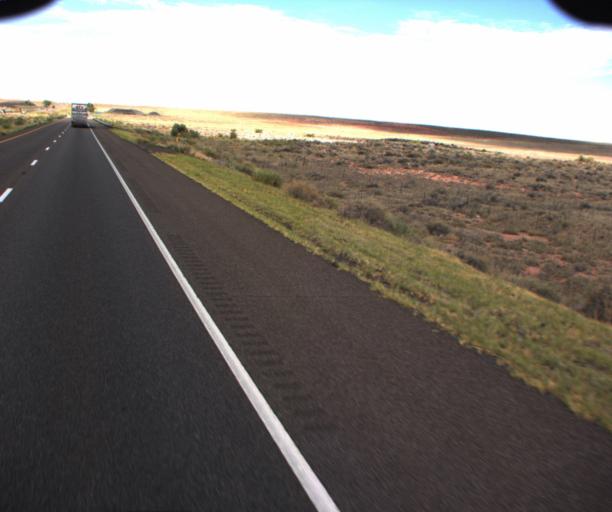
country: US
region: Arizona
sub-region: Navajo County
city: Holbrook
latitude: 35.0859
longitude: -109.7030
